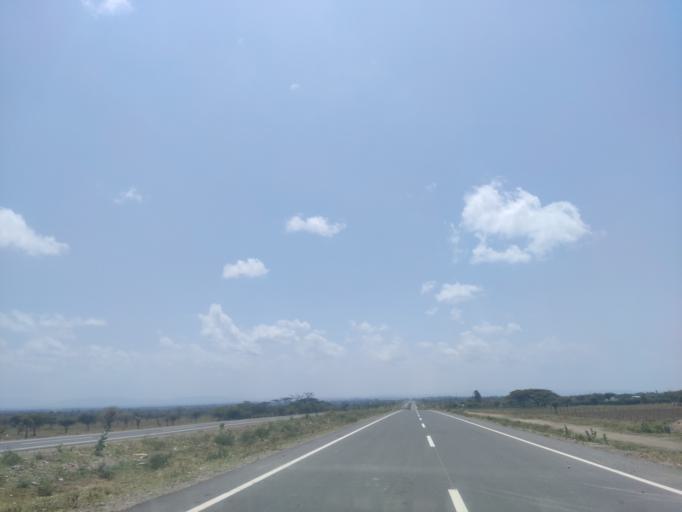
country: ET
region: Oromiya
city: Mojo
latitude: 8.3622
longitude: 38.9912
